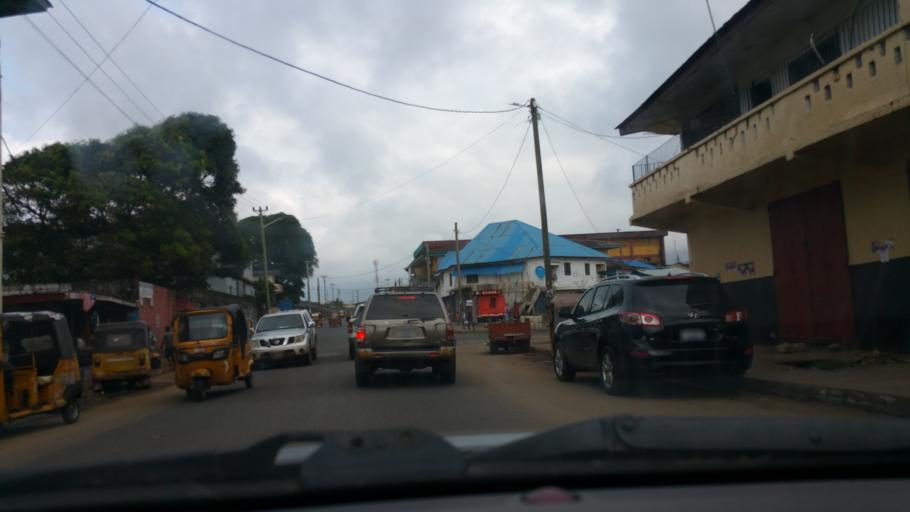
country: LR
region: Montserrado
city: Monrovia
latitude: 6.3070
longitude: -10.8011
